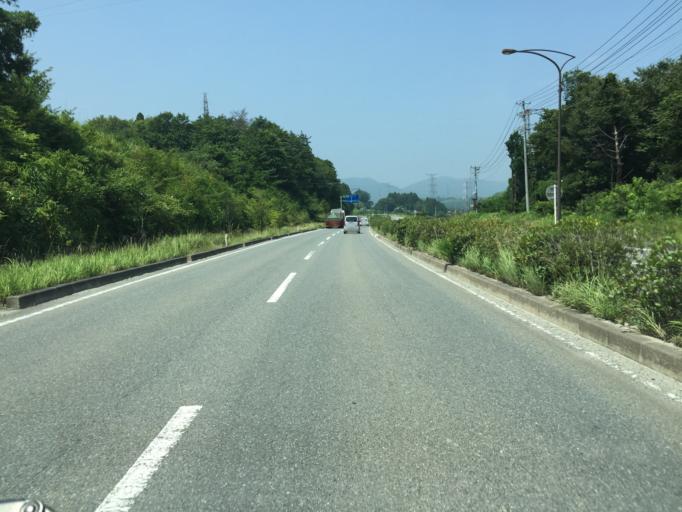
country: JP
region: Miyagi
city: Marumori
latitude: 37.8381
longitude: 140.9147
